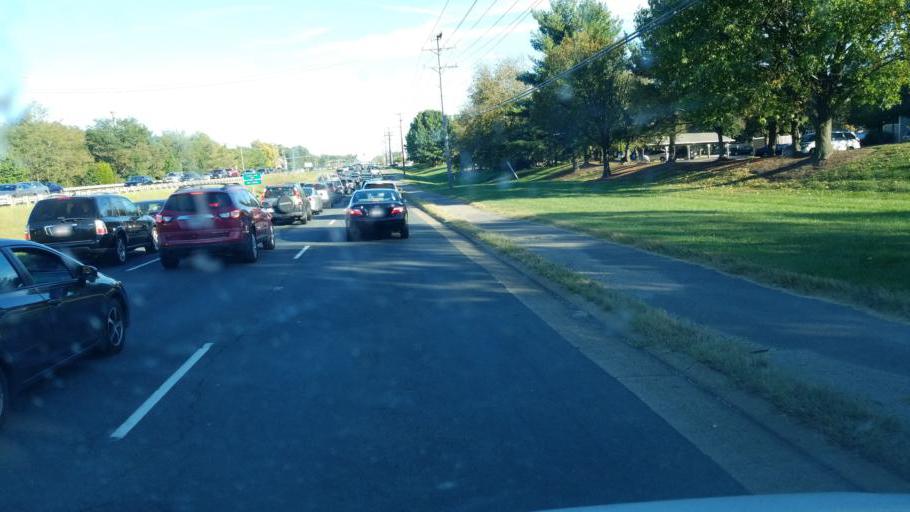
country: US
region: Virginia
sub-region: Fairfax County
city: Greenbriar
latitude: 38.8834
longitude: -77.4040
